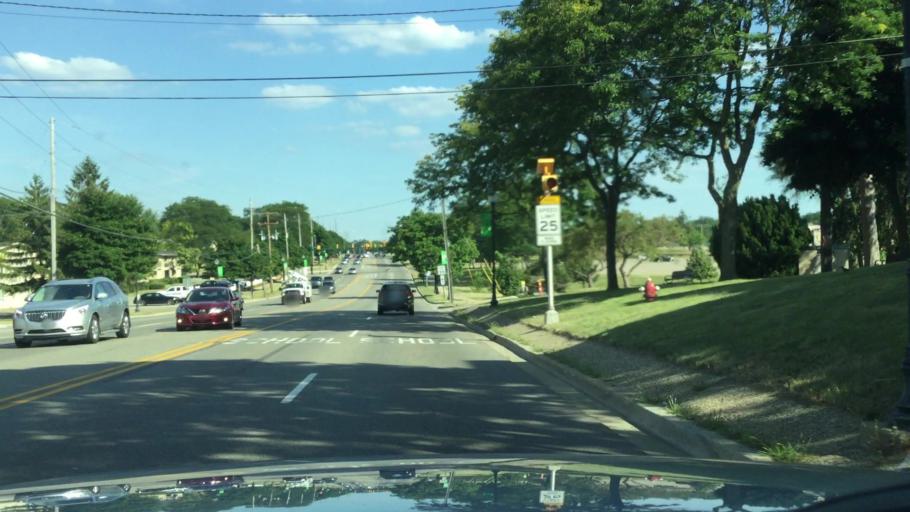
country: US
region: Michigan
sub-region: Genesee County
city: Grand Blanc
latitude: 42.9237
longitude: -83.6256
